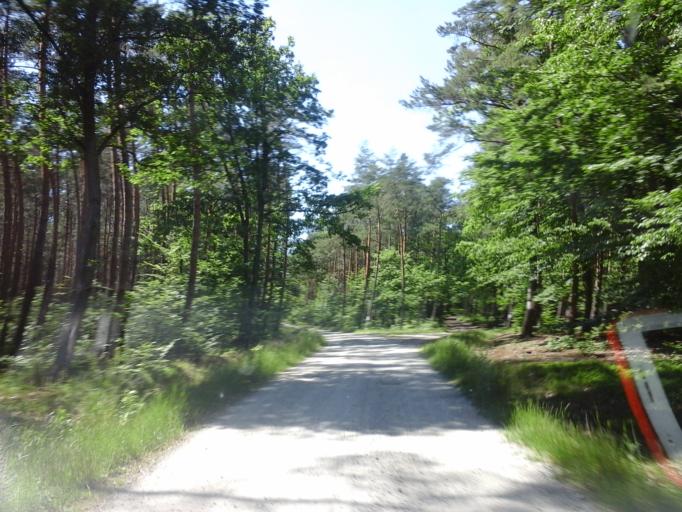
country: PL
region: West Pomeranian Voivodeship
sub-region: Powiat choszczenski
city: Bierzwnik
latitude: 53.0856
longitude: 15.7641
